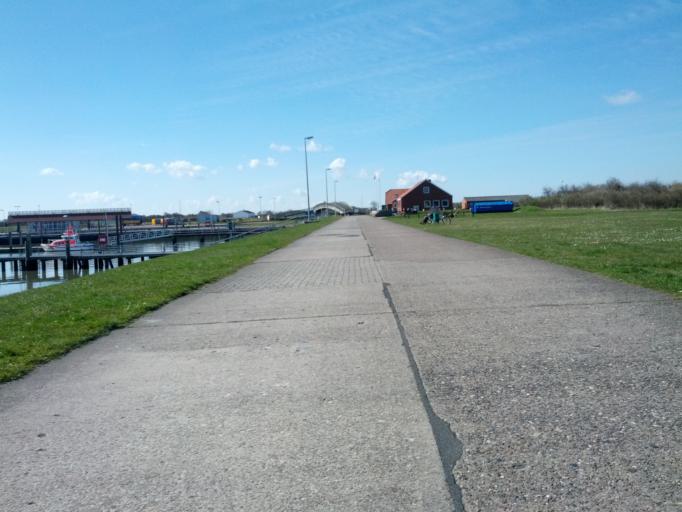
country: DE
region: Lower Saxony
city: Langeoog
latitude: 53.7276
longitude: 7.4960
